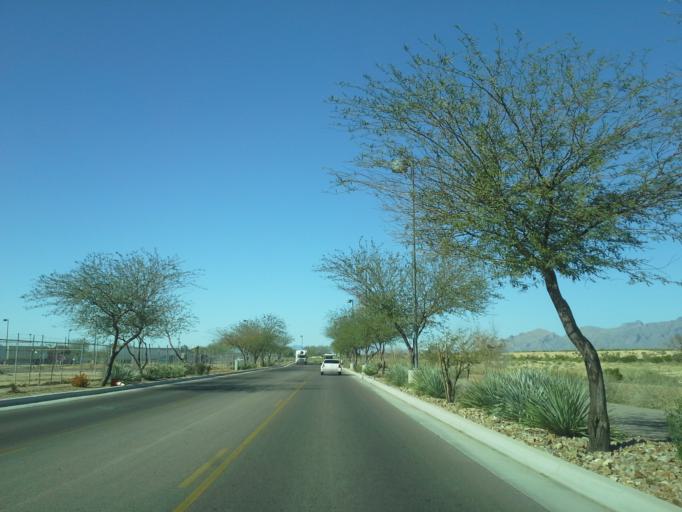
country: US
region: Arizona
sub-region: Pima County
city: South Tucson
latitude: 32.1846
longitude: -110.9505
